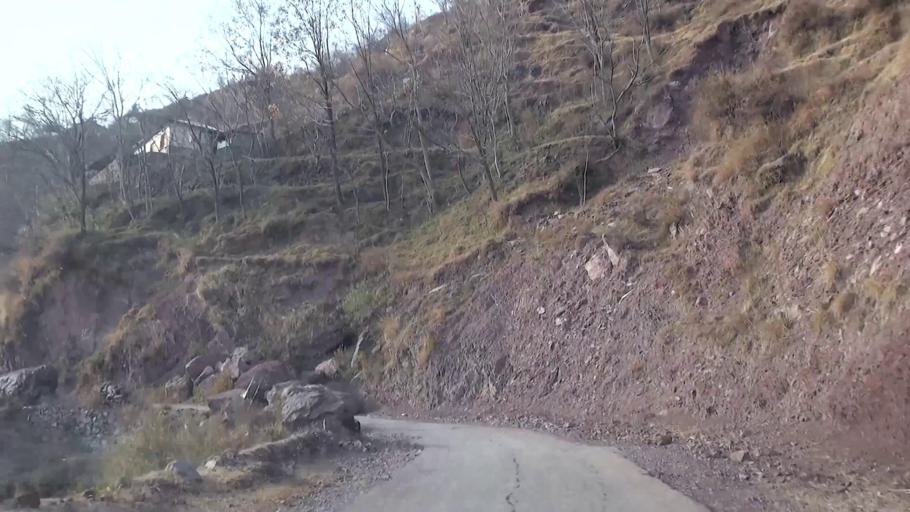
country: PK
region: Azad Kashmir
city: Muzaffarabad
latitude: 34.3697
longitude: 73.5183
